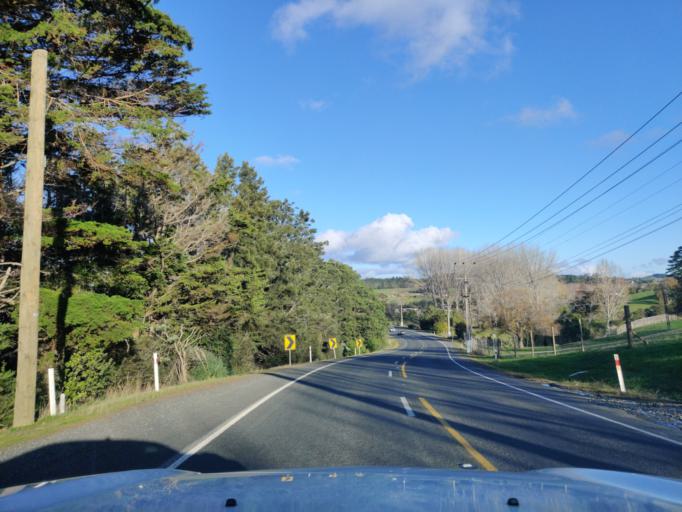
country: NZ
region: Auckland
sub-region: Auckland
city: Pakuranga
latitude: -36.9538
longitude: 174.9683
